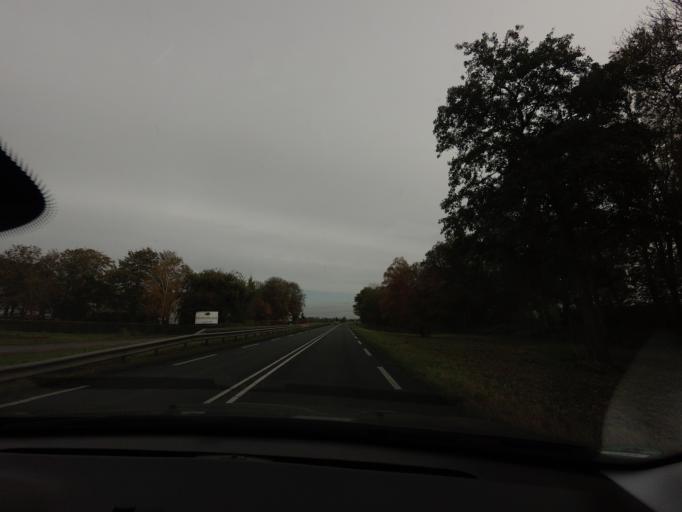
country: NL
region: Flevoland
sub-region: Gemeente Noordoostpolder
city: Emmeloord
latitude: 52.7090
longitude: 5.8166
